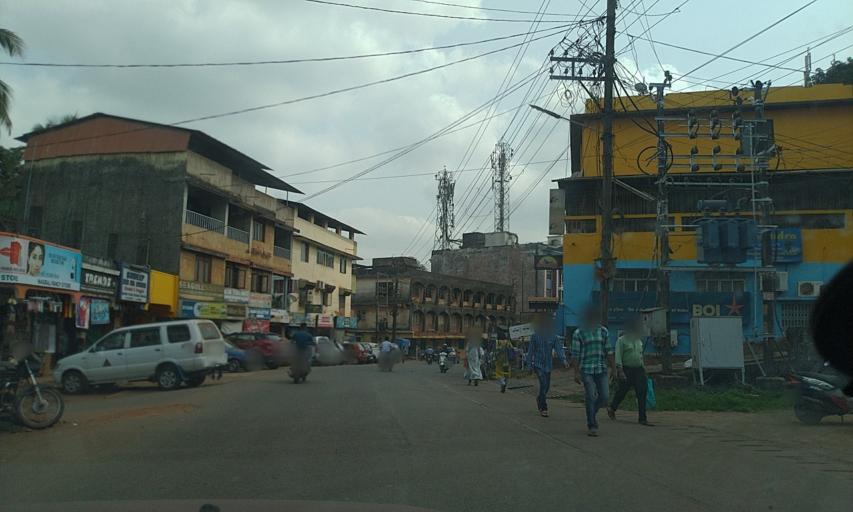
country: IN
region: Goa
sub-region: North Goa
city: Ponda
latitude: 15.4010
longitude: 74.0058
